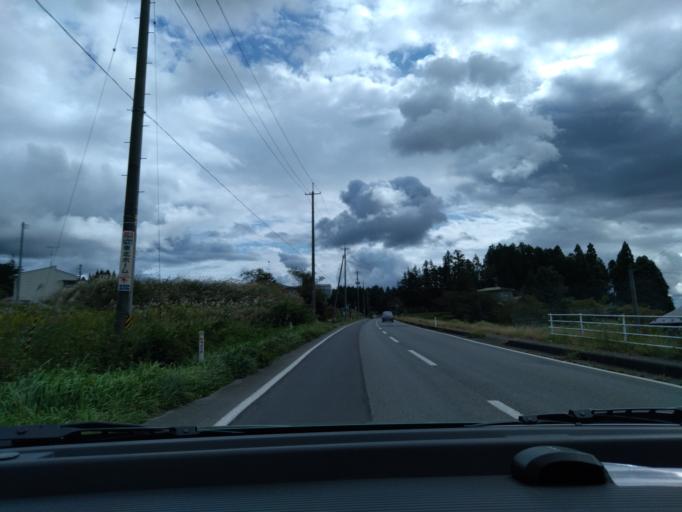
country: JP
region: Iwate
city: Ichinoseki
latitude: 38.8539
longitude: 141.1720
